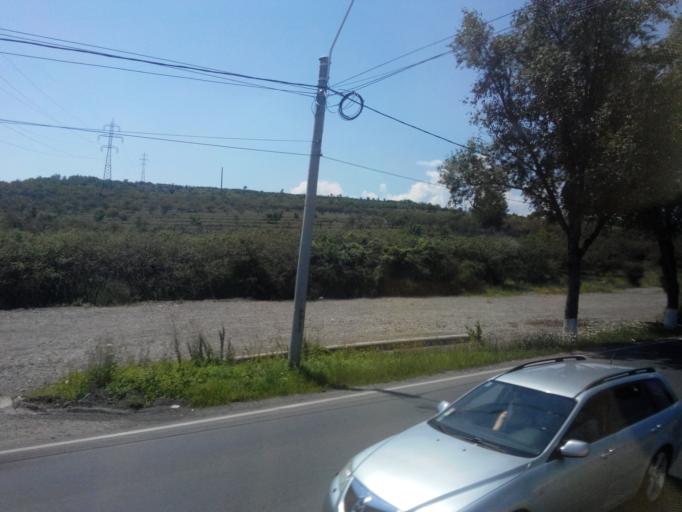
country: RO
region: Hunedoara
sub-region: Municipiul Deva
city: Cristur
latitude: 45.8592
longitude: 22.9373
